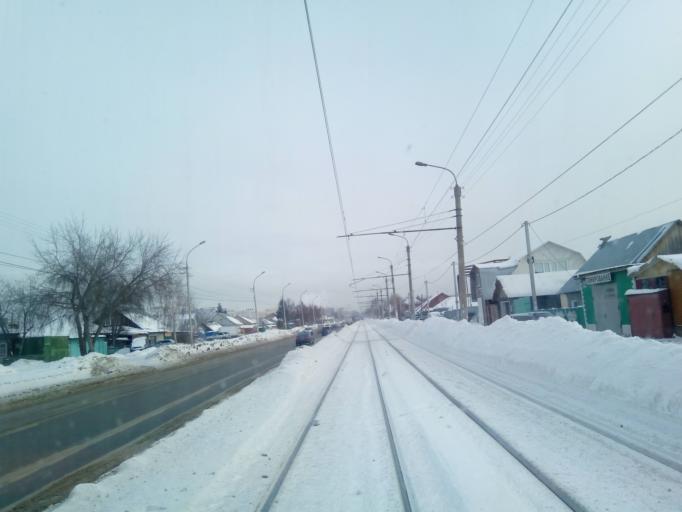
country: RU
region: Novosibirsk
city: Tolmachevo
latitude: 54.9807
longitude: 82.8430
